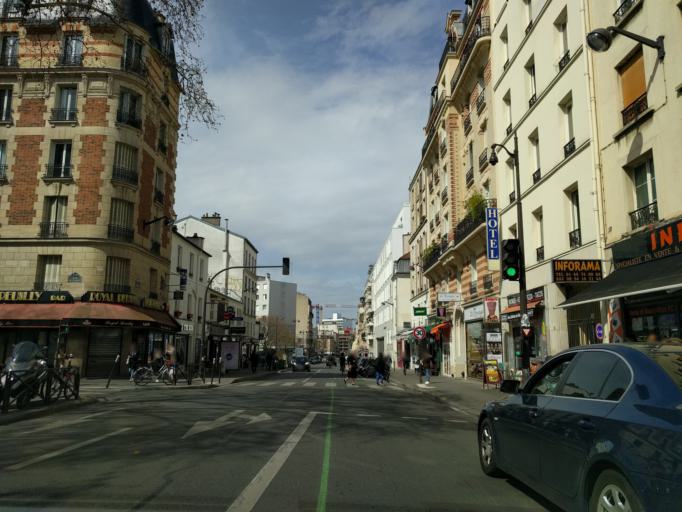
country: FR
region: Ile-de-France
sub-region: Departement du Val-de-Marne
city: Saint-Mande
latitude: 48.8444
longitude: 2.3901
